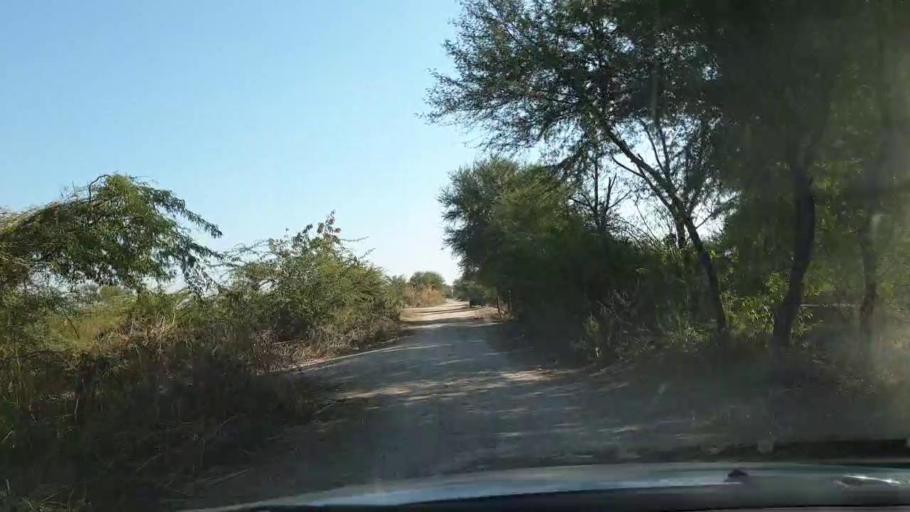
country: PK
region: Sindh
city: Jhol
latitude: 25.9182
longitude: 68.9635
